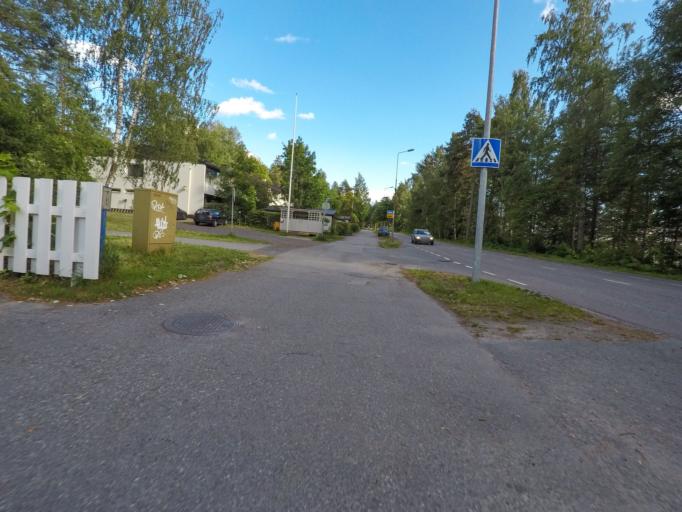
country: FI
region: South Karelia
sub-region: Lappeenranta
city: Lappeenranta
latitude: 61.0682
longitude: 28.1565
